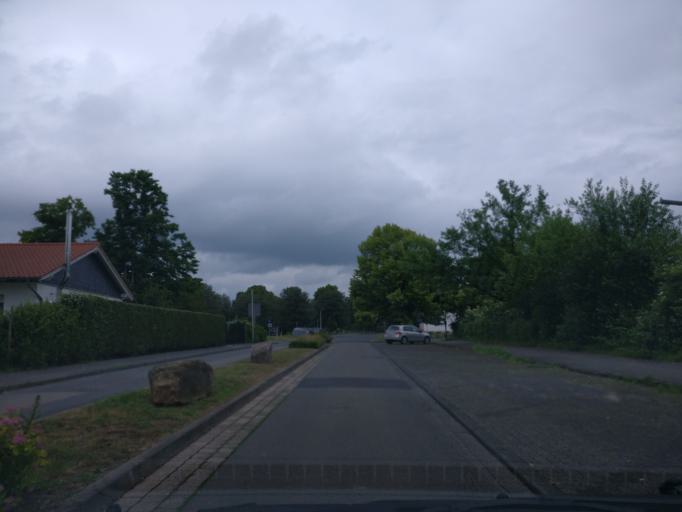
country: DE
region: Hesse
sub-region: Regierungsbezirk Kassel
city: Fuldatal
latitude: 51.3556
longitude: 9.5333
